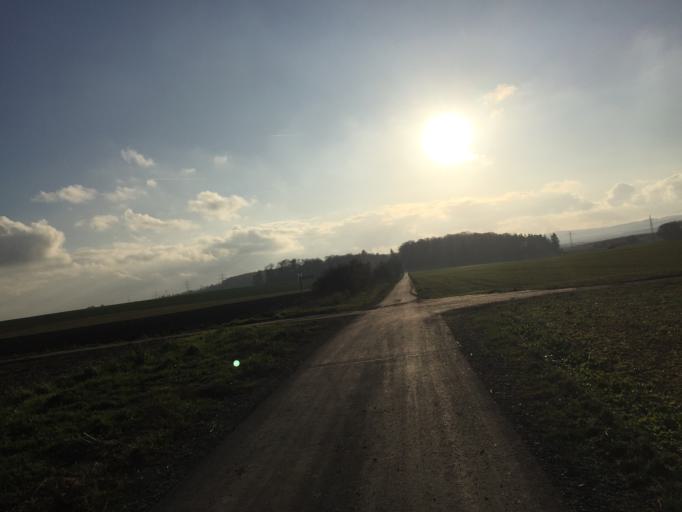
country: DE
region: Hesse
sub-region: Regierungsbezirk Giessen
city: Langgons
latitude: 50.5099
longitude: 8.7070
